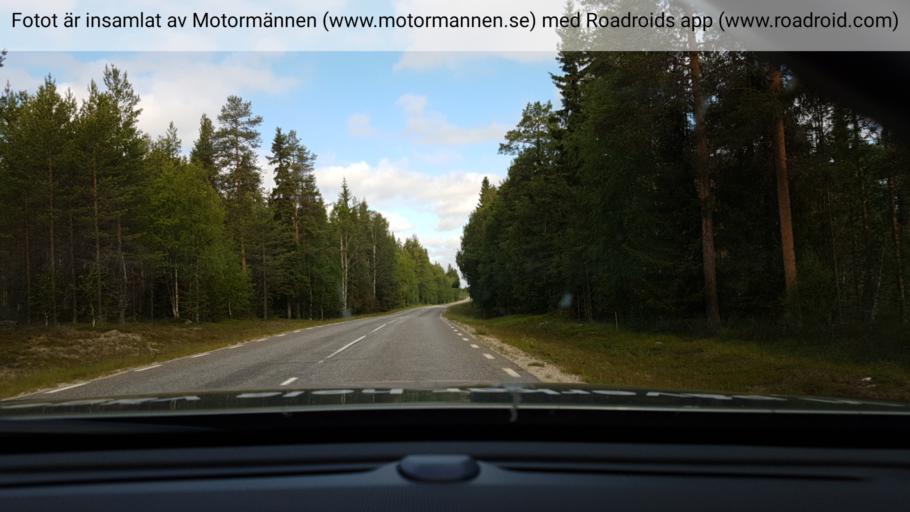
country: SE
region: Vaesterbotten
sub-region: Norsjo Kommun
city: Norsjoe
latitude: 64.7401
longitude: 19.1171
